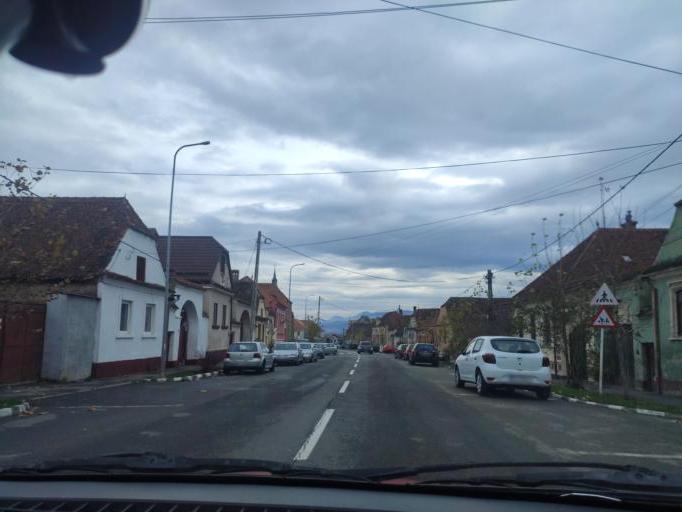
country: RO
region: Brasov
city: Codlea
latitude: 45.7011
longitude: 25.4425
